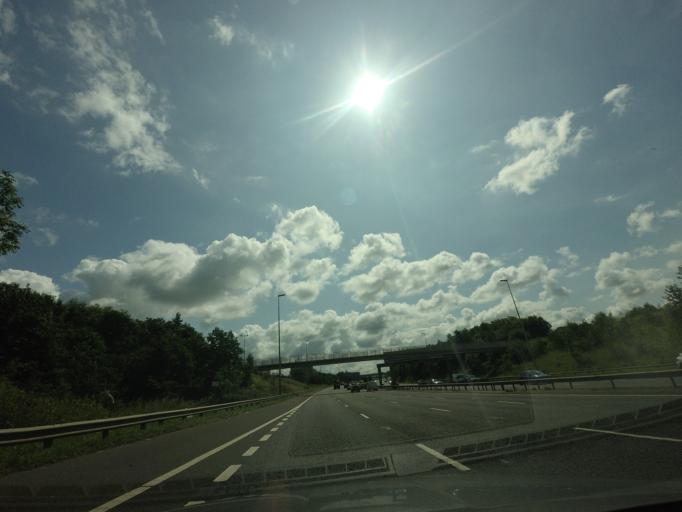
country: GB
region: England
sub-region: Lancashire
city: Goosnargh
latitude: 53.7866
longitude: -2.6538
